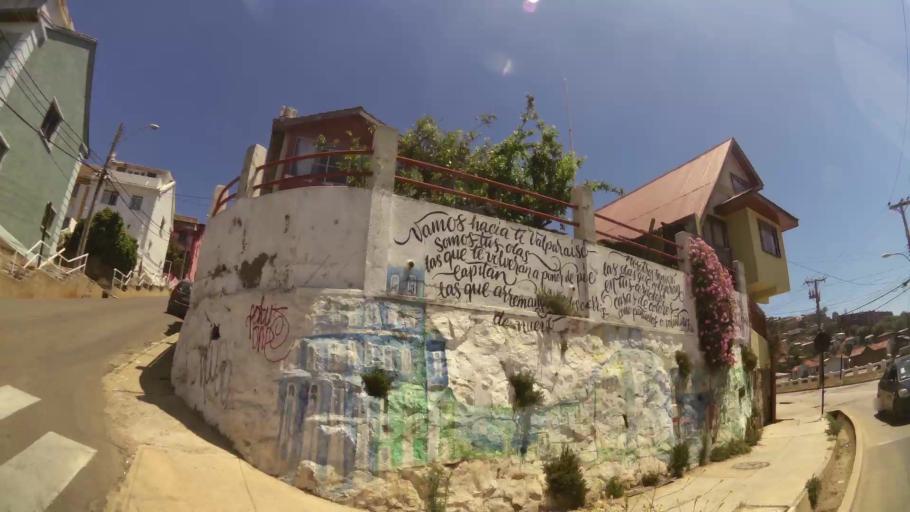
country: CL
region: Valparaiso
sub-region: Provincia de Valparaiso
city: Valparaiso
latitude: -33.0516
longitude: -71.6271
